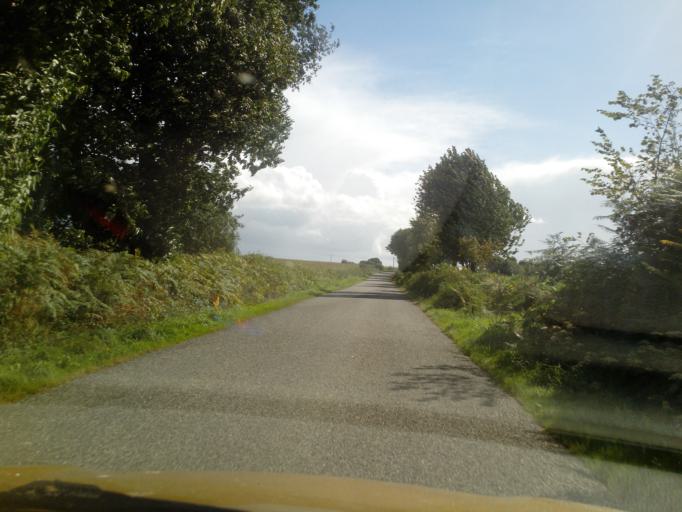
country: FR
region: Brittany
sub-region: Departement des Cotes-d'Armor
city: Merdrignac
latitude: 48.1668
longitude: -2.4185
